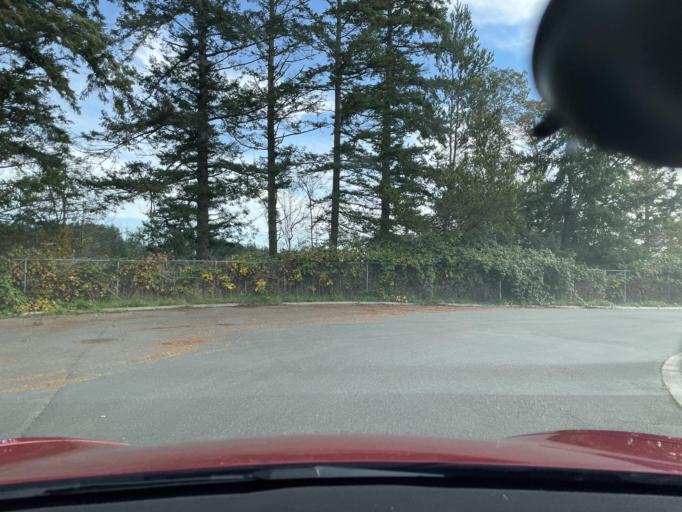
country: US
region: Washington
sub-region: San Juan County
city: Friday Harbor
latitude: 48.5424
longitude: -123.0304
